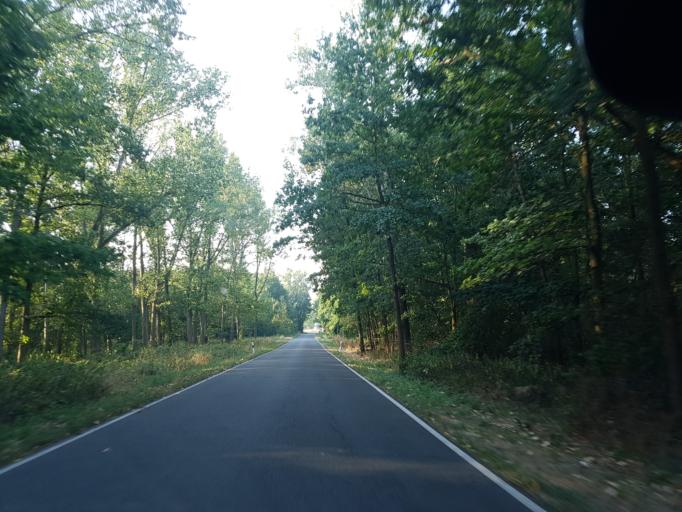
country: DE
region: Saxony
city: Strehla
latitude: 51.3156
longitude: 13.1937
